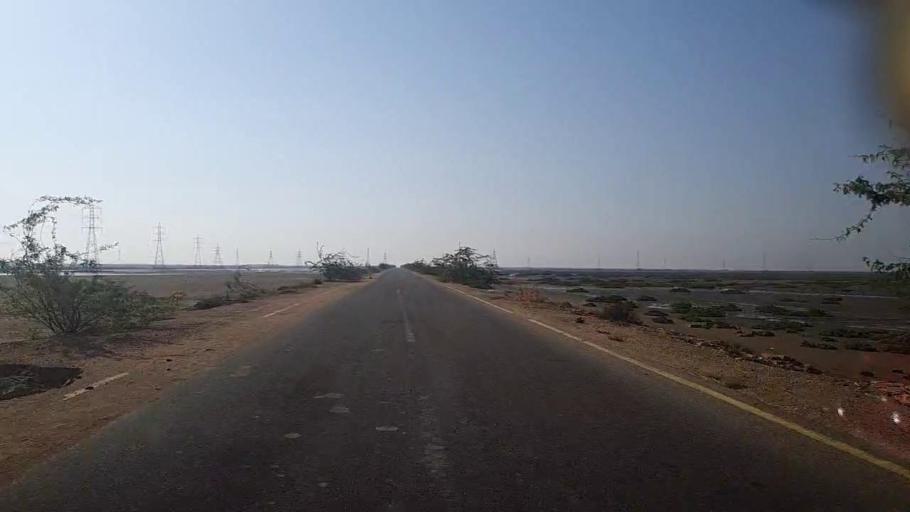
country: PK
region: Sindh
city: Mirpur Sakro
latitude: 24.5989
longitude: 67.4981
